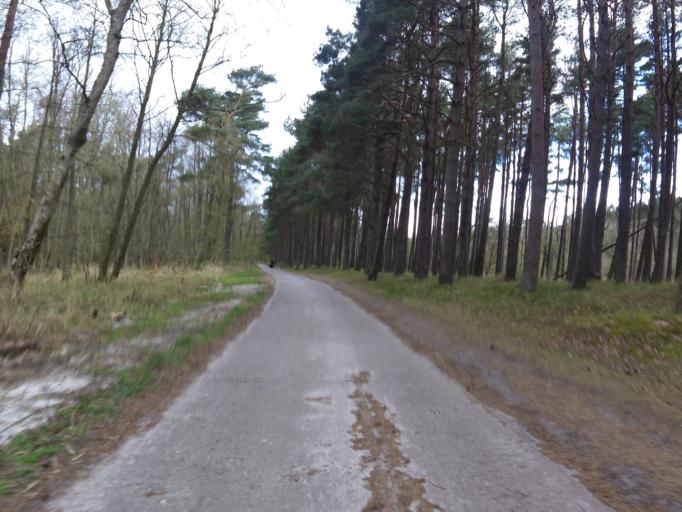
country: DE
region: Mecklenburg-Vorpommern
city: Ostseebad Prerow
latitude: 54.4620
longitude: 12.5300
